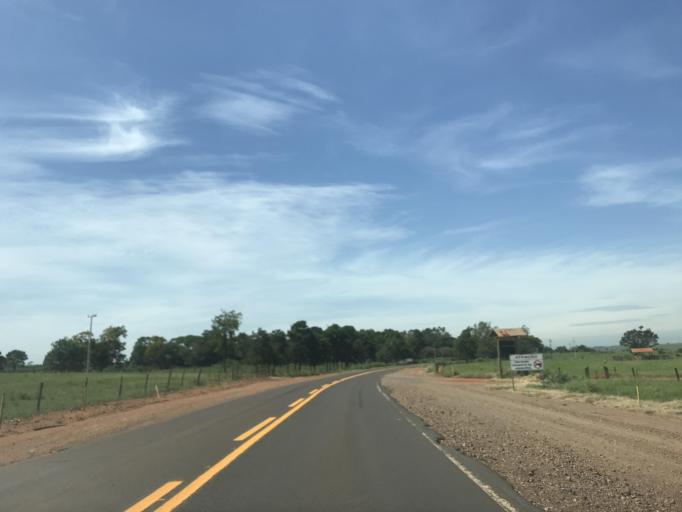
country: BR
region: Parana
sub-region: Terra Rica
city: Terra Rica
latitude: -22.7931
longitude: -52.6533
